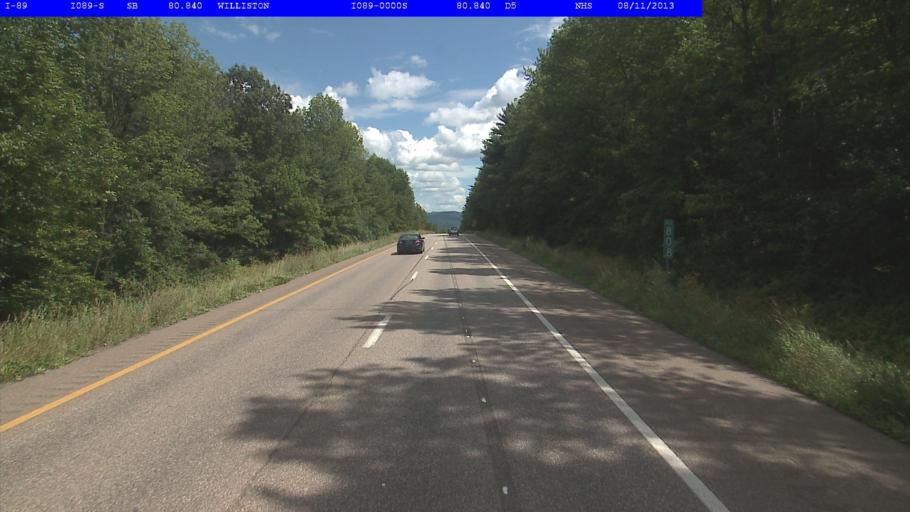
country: US
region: Vermont
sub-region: Chittenden County
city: Williston
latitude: 44.4330
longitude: -73.0530
